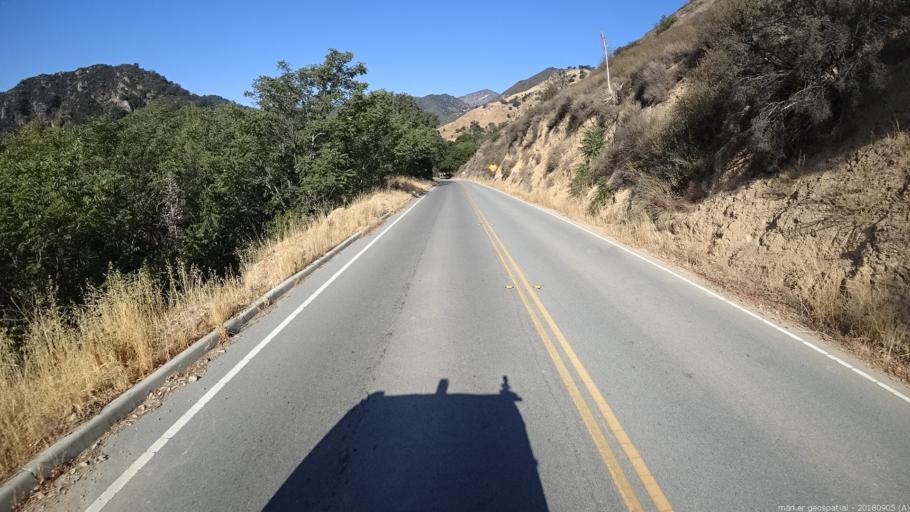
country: US
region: California
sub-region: Monterey County
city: Soledad
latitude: 36.2364
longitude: -121.4727
